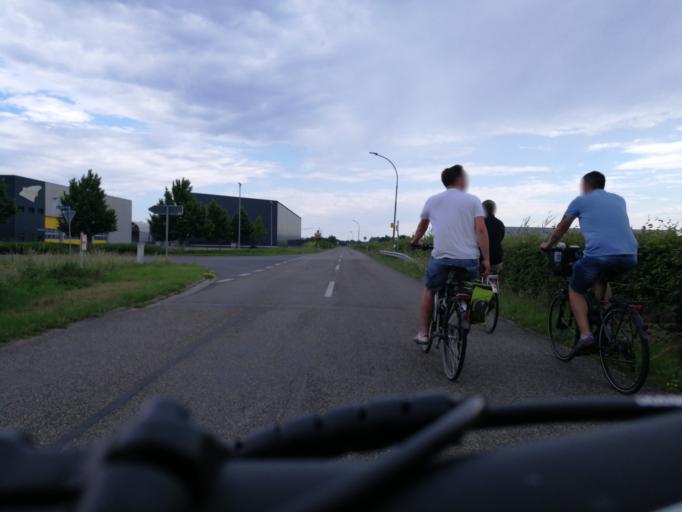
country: DE
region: North Rhine-Westphalia
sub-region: Regierungsbezirk Dusseldorf
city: Kleve
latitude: 51.8164
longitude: 6.1430
